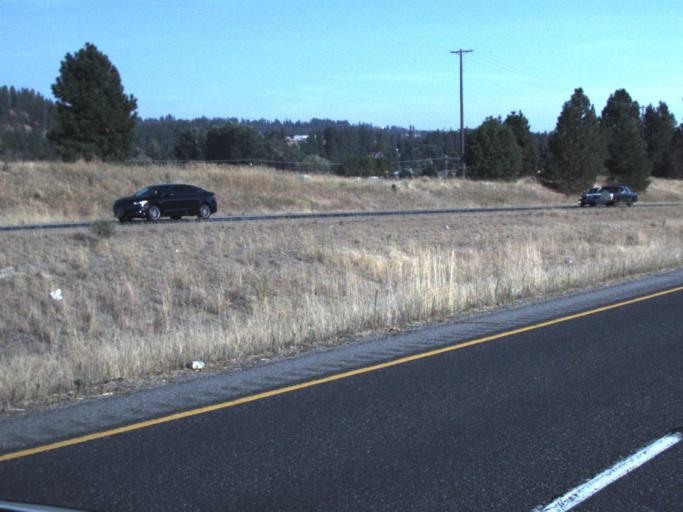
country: US
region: Washington
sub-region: Spokane County
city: Mead
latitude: 47.8312
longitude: -117.3523
